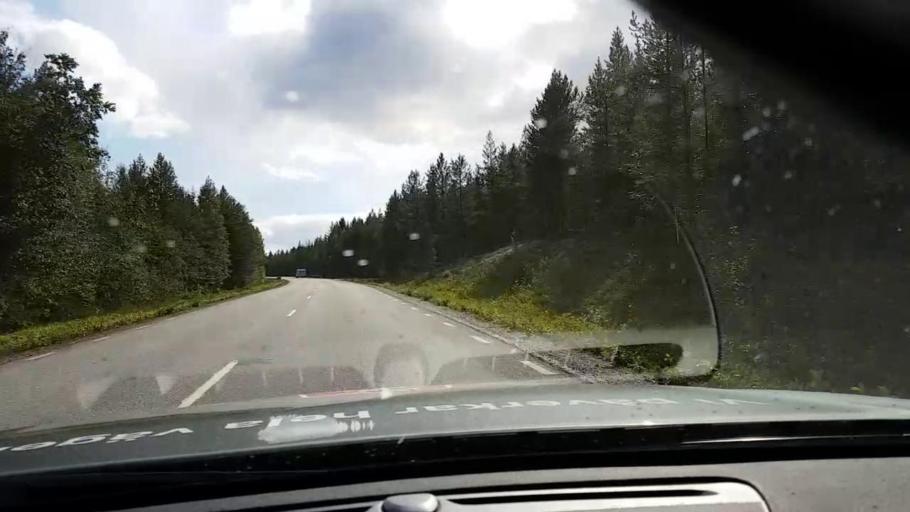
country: SE
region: Vaesternorrland
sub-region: OErnskoeldsviks Kommun
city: Bredbyn
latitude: 63.6255
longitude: 17.9082
